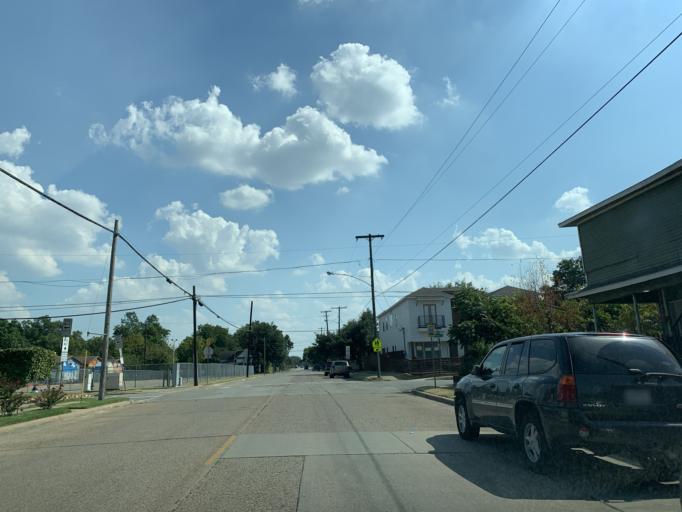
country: US
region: Texas
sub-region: Dallas County
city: Dallas
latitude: 32.7476
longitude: -96.8321
